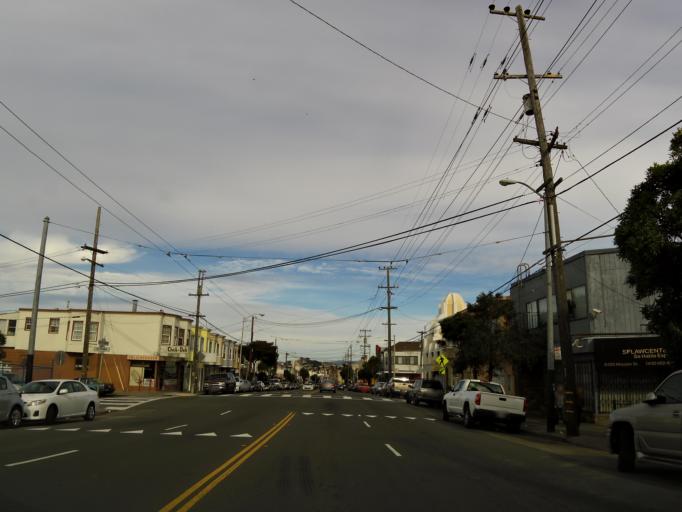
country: US
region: California
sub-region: San Mateo County
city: Daly City
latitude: 37.7134
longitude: -122.4440
